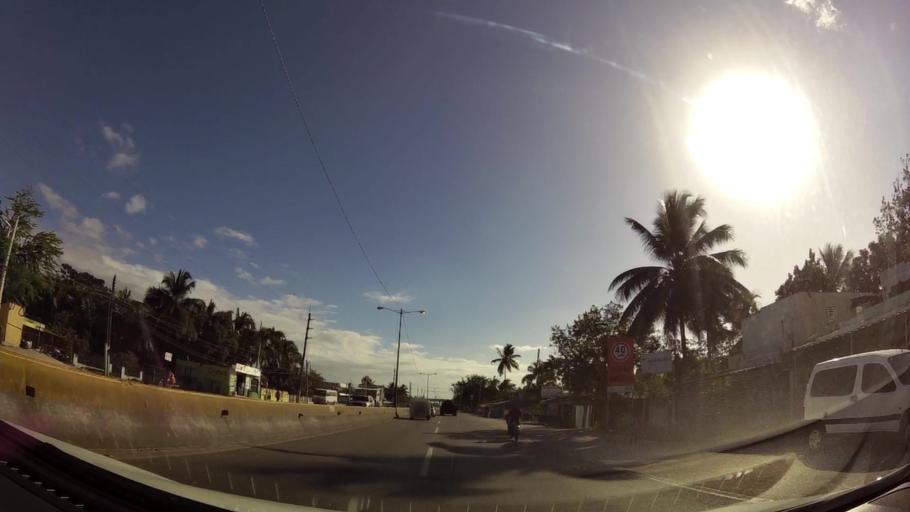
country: DO
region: Santo Domingo
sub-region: Santo Domingo
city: Boca Chica
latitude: 18.4494
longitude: -69.6315
